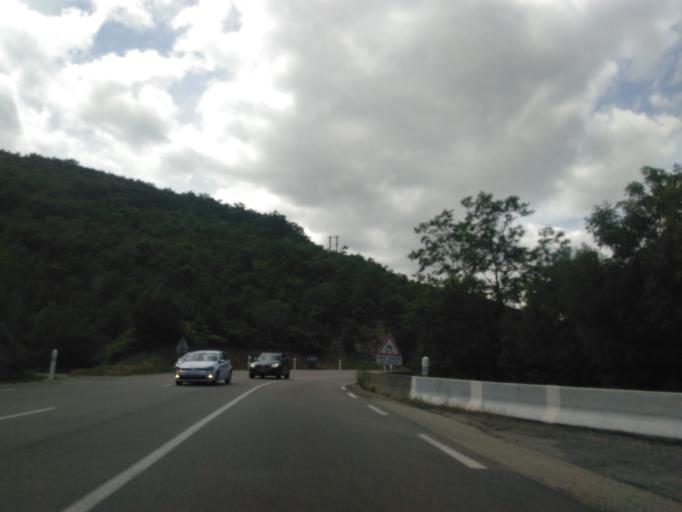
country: FR
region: Rhone-Alpes
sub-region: Departement de l'Ardeche
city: Le Teil
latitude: 44.5641
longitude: 4.6435
